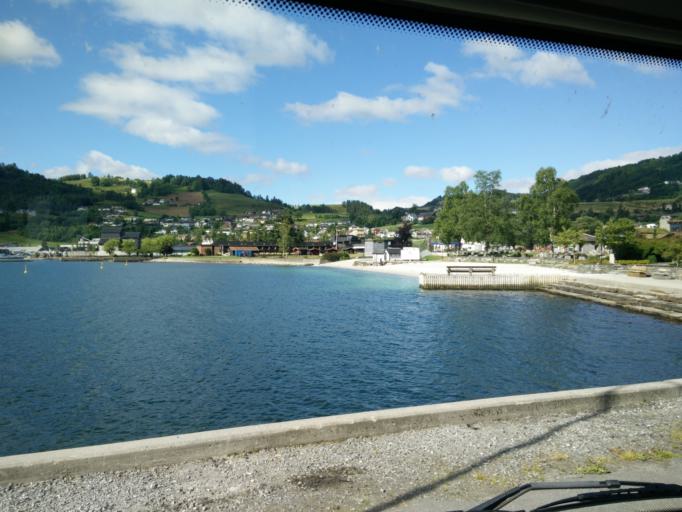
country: NO
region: Hordaland
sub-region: Kvam
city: Oystese
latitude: 60.3874
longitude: 6.2058
